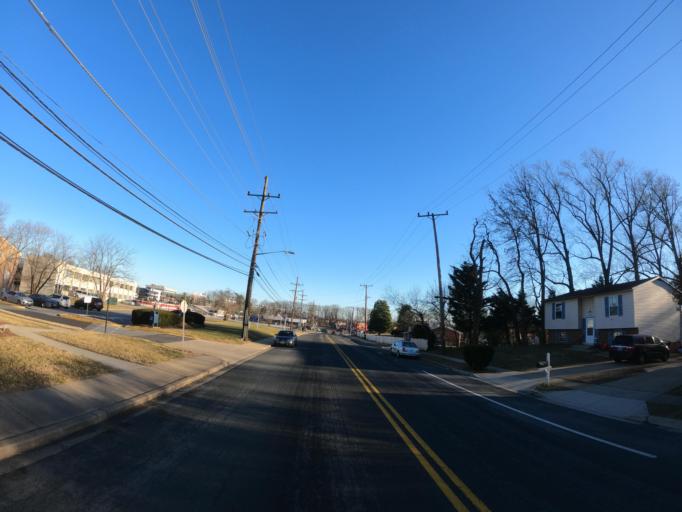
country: US
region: Maryland
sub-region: Prince George's County
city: Woodlawn
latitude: 38.9542
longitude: -76.8796
